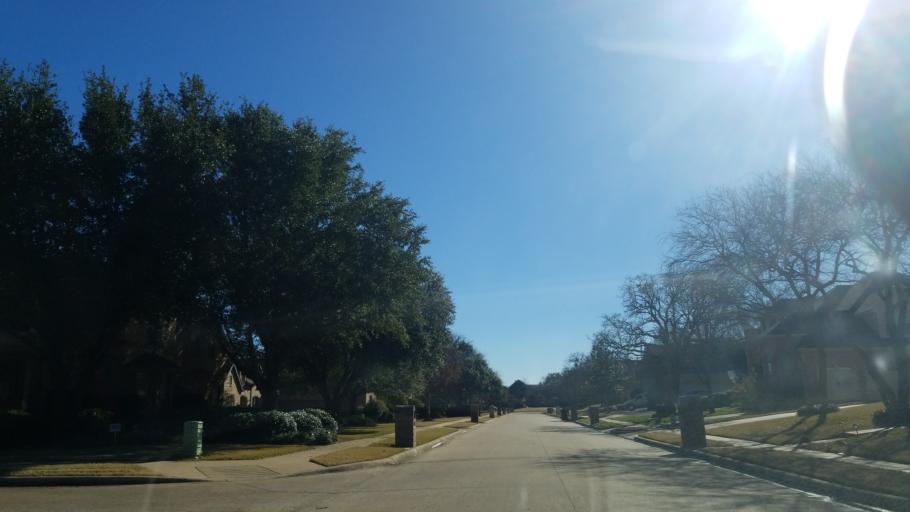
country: US
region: Texas
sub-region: Denton County
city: Corinth
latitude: 33.1542
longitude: -97.0858
